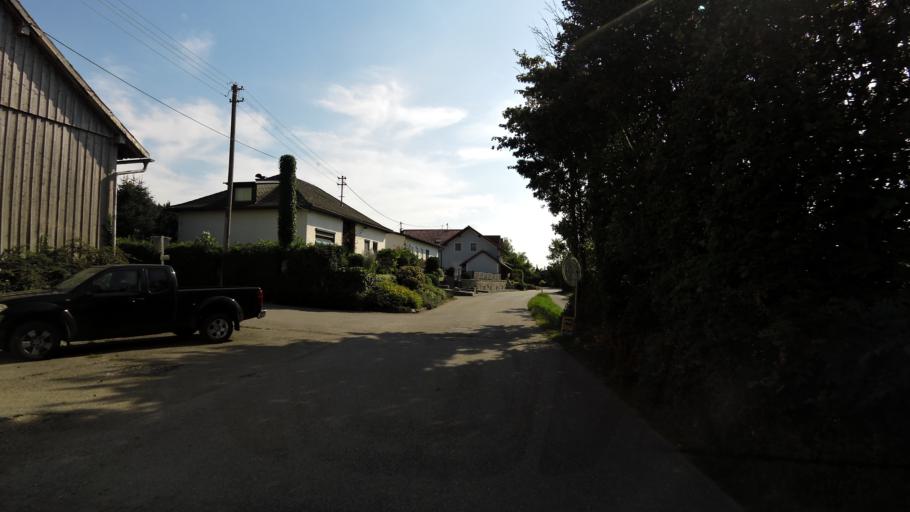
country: DE
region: Bavaria
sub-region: Lower Bavaria
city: Stubenberg
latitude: 48.2683
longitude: 13.0995
